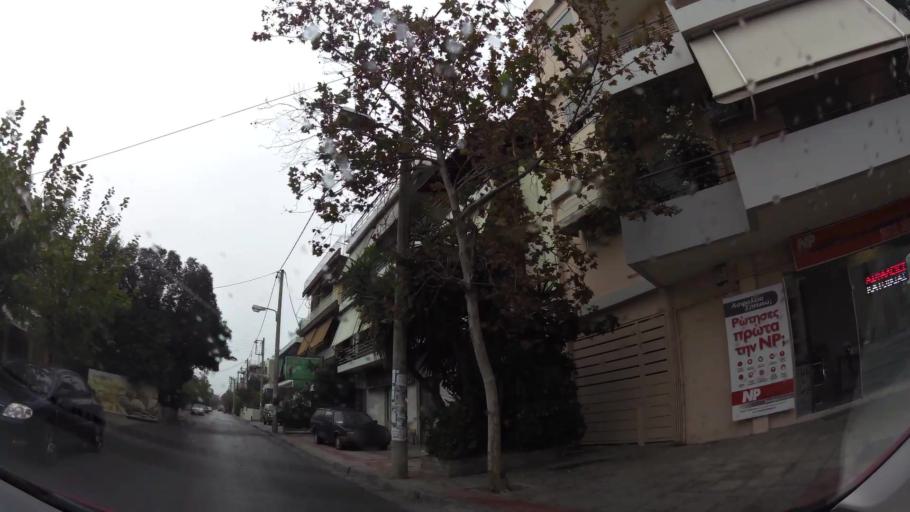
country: GR
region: Attica
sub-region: Nomarchia Athinas
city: Agioi Anargyroi
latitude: 38.0267
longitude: 23.7249
